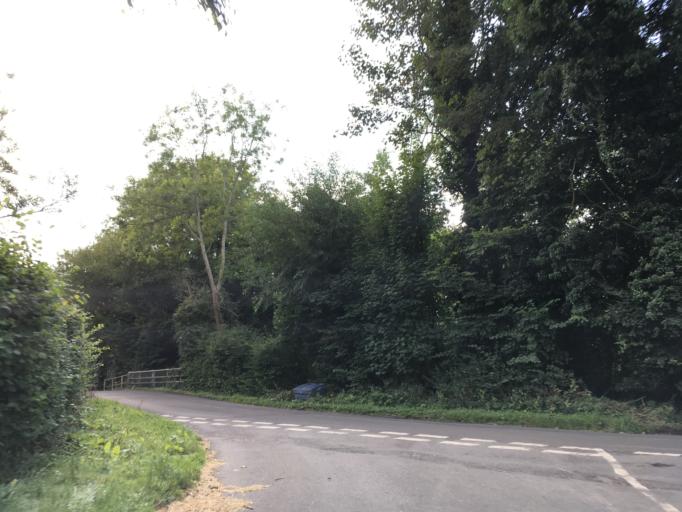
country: GB
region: England
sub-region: Hampshire
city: Andover
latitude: 51.1923
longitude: -1.3815
